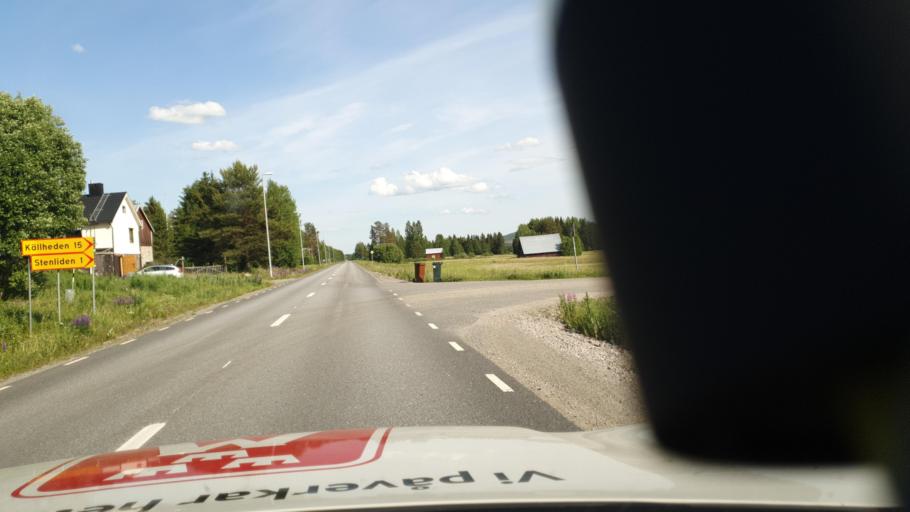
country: SE
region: Vaesterbotten
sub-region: Skelleftea Kommun
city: Forsbacka
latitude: 64.7038
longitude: 20.4464
